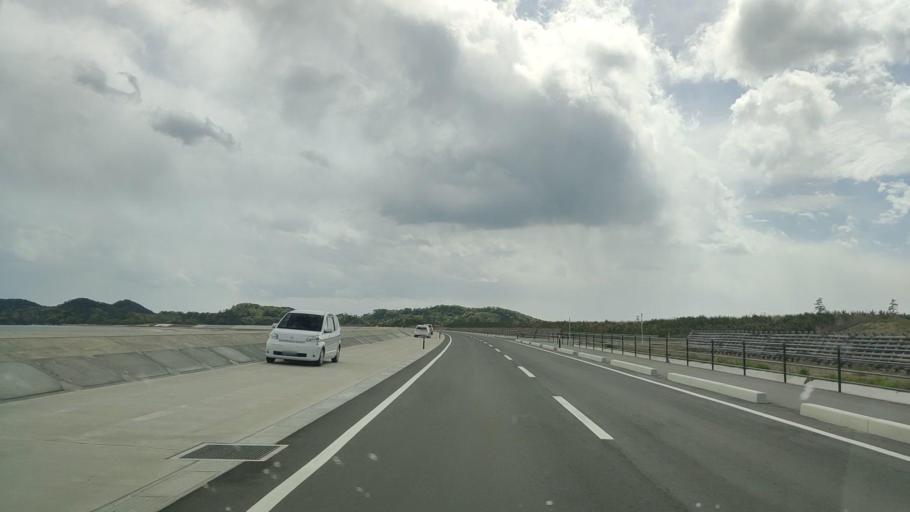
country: JP
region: Miyagi
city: Yamoto
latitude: 38.3698
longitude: 141.1631
